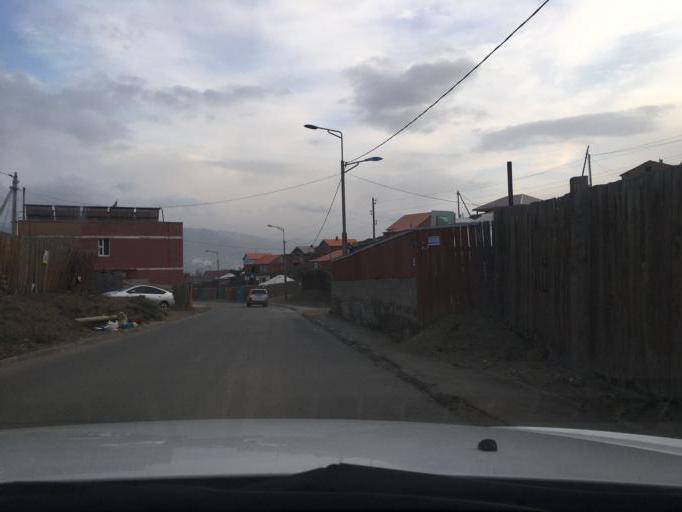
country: MN
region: Ulaanbaatar
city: Ulaanbaatar
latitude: 47.9309
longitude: 106.8582
